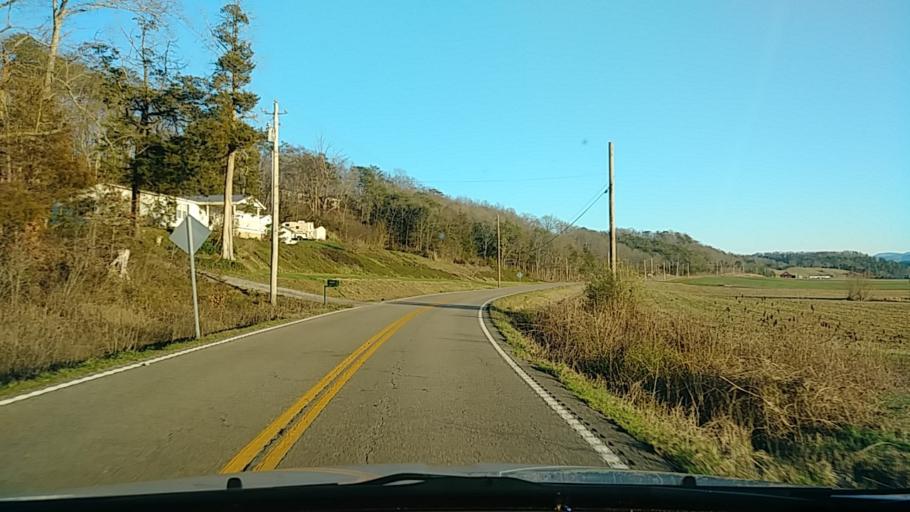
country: US
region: Tennessee
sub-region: Greene County
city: Mosheim
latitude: 36.1210
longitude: -83.0850
